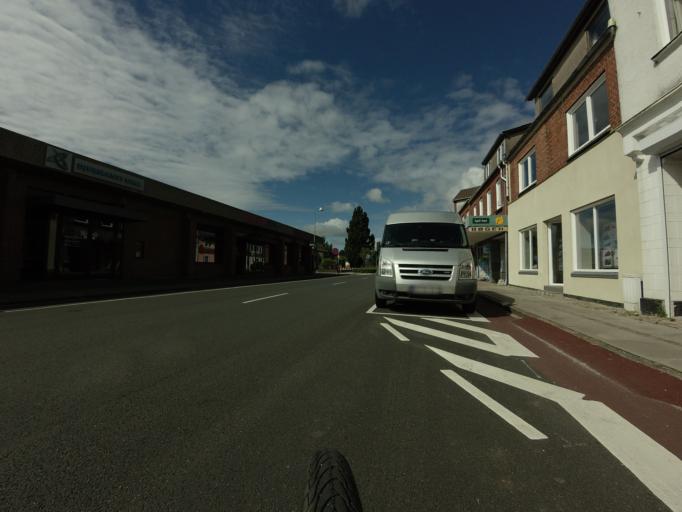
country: DK
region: Central Jutland
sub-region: Norddjurs Kommune
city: Allingabro
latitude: 56.4639
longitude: 10.3234
